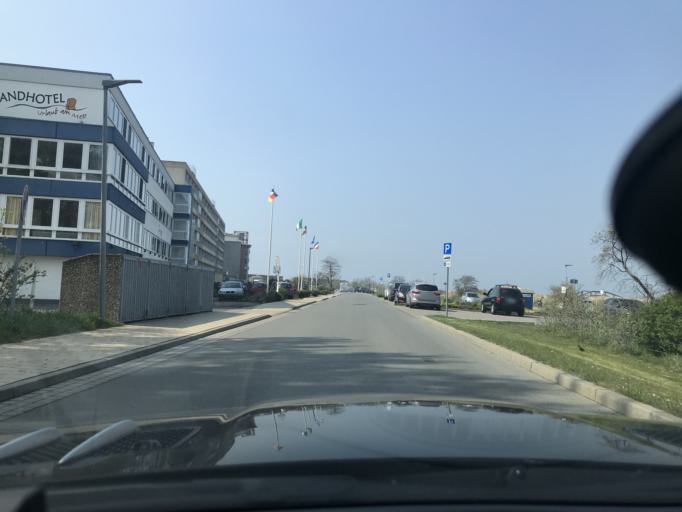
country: DE
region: Schleswig-Holstein
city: Heiligenhafen
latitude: 54.3815
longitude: 10.9572
